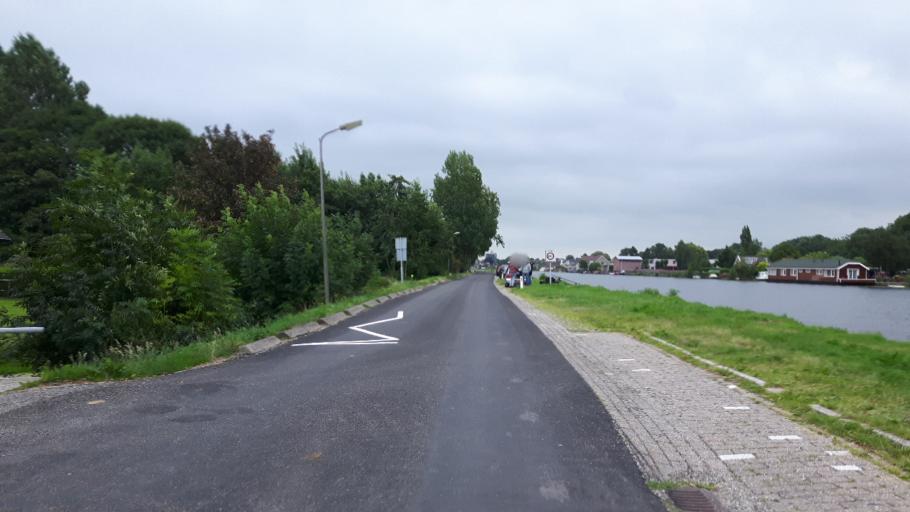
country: NL
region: South Holland
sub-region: Bodegraven-Reeuwijk
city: Bodegraven
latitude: 52.1100
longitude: 4.7168
